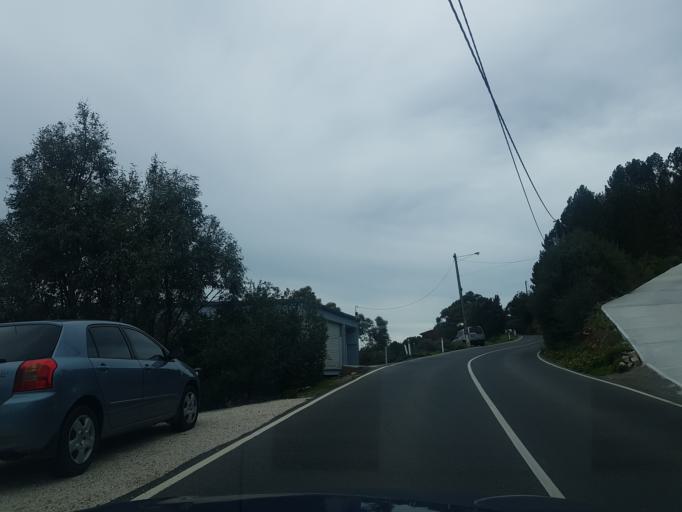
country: AU
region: South Australia
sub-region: Burnside
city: Mount Osmond
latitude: -34.9621
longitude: 138.6500
